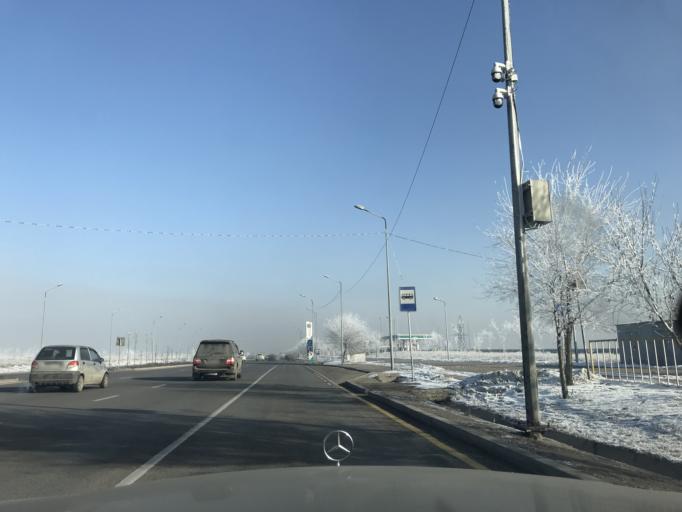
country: KZ
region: Almaty Oblysy
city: Burunday
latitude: 43.2939
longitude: 76.8313
